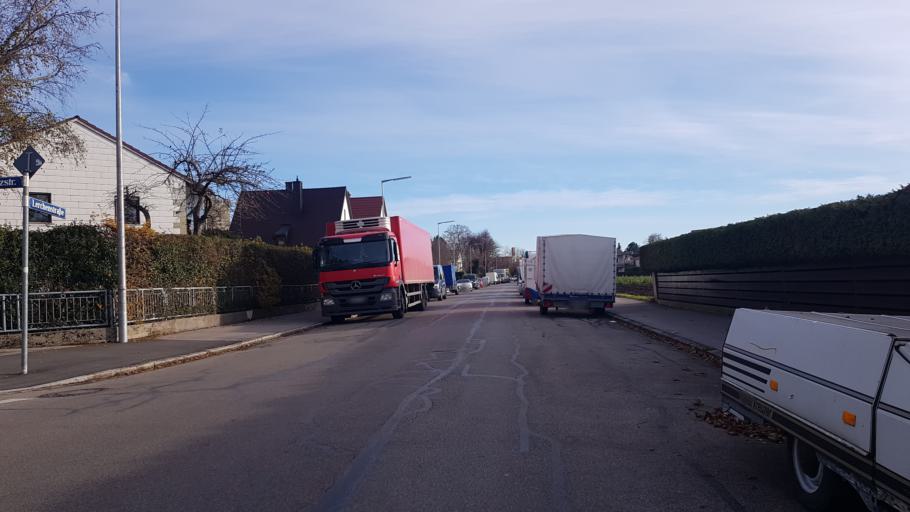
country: DE
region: Bavaria
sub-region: Upper Bavaria
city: Oberschleissheim
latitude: 48.2121
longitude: 11.5370
